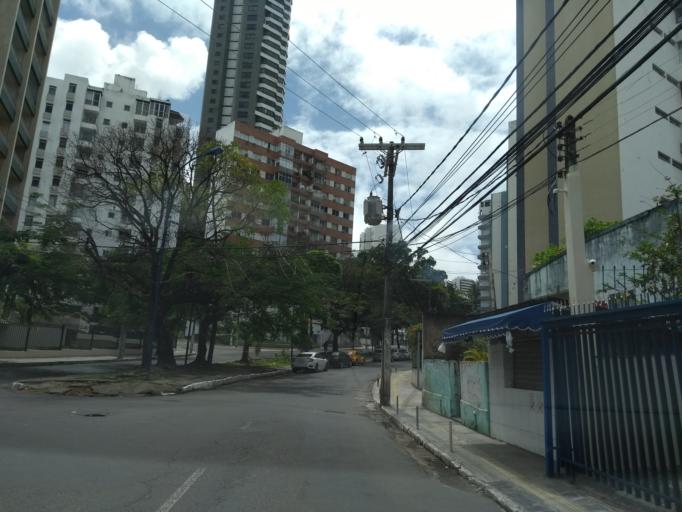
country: BR
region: Bahia
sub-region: Salvador
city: Salvador
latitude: -13.0054
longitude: -38.5213
